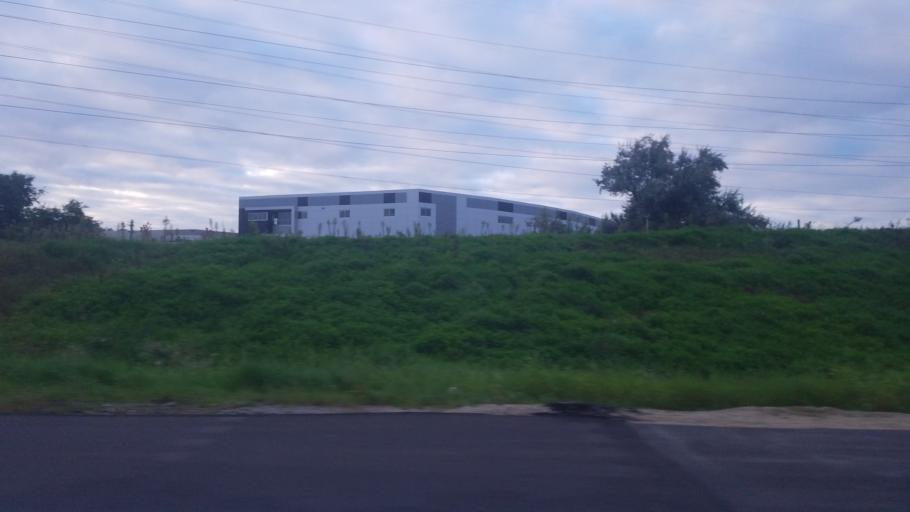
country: US
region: Minnesota
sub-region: Ramsey County
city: Lauderdale
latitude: 45.0101
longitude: -93.2028
